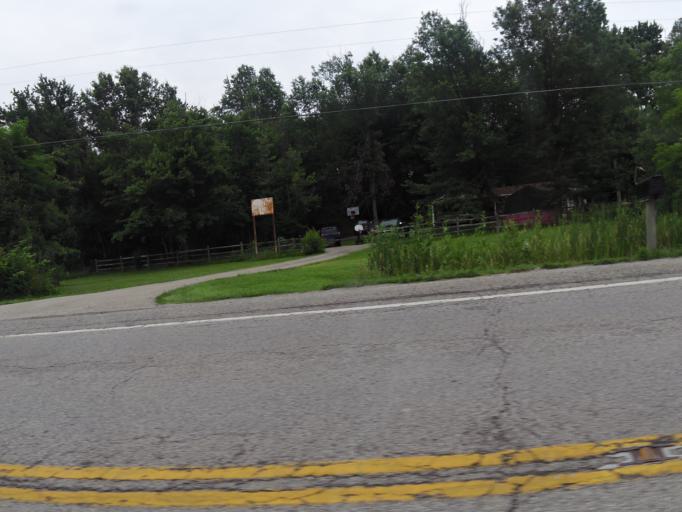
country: US
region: Ohio
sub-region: Brown County
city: Mount Orab
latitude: 39.0744
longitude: -83.9251
